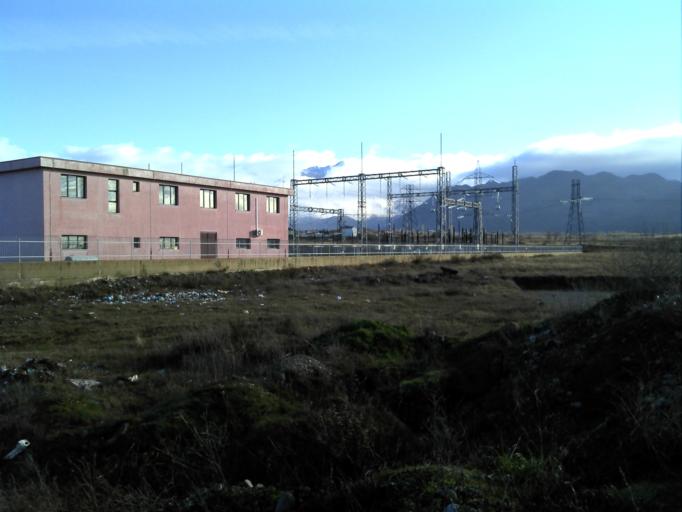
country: AL
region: Shkoder
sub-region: Rrethi i Malesia e Madhe
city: Koplik
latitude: 42.2115
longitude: 19.4555
